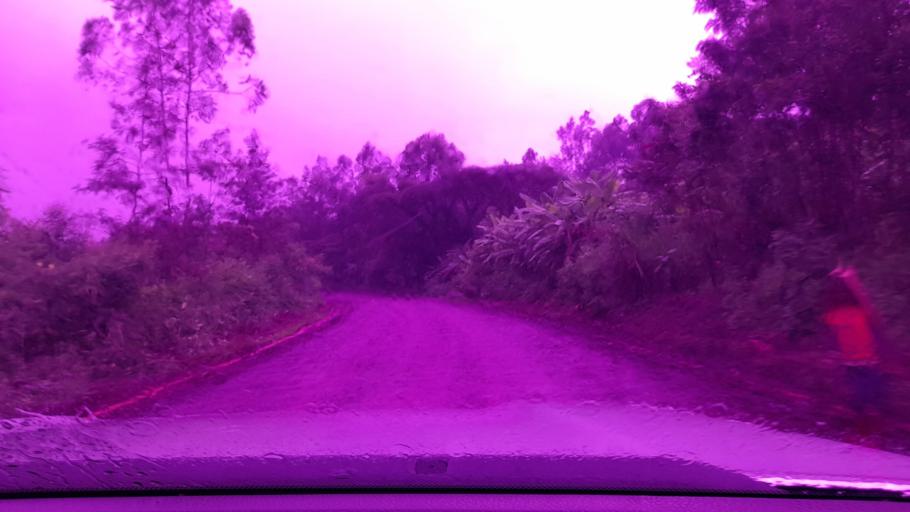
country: ET
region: Oromiya
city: Metu
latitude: 8.3340
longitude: 35.6060
